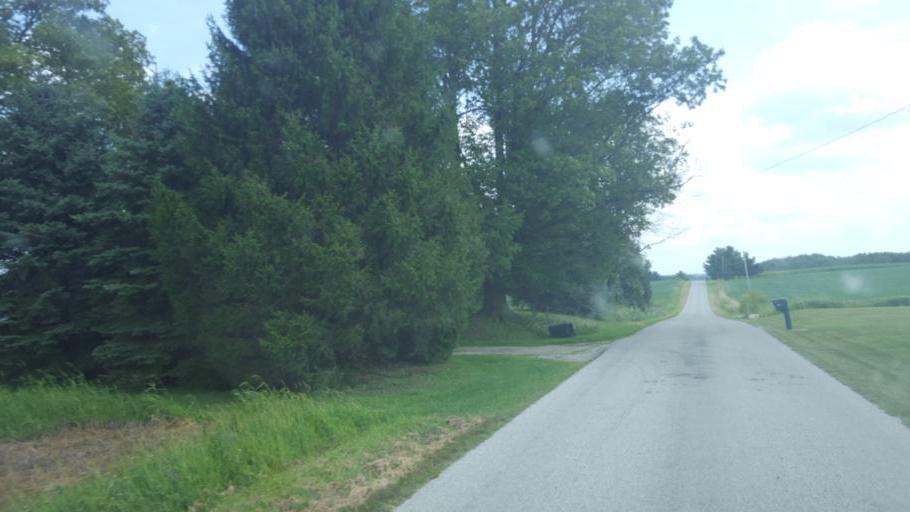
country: US
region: Ohio
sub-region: Richland County
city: Lexington
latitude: 40.6382
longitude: -82.7033
